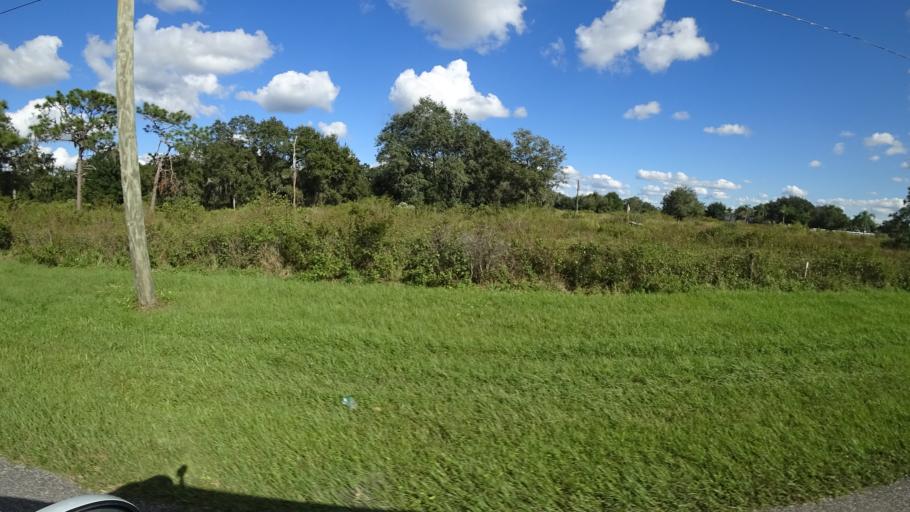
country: US
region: Florida
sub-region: Sarasota County
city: Lake Sarasota
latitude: 27.3653
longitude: -82.2684
